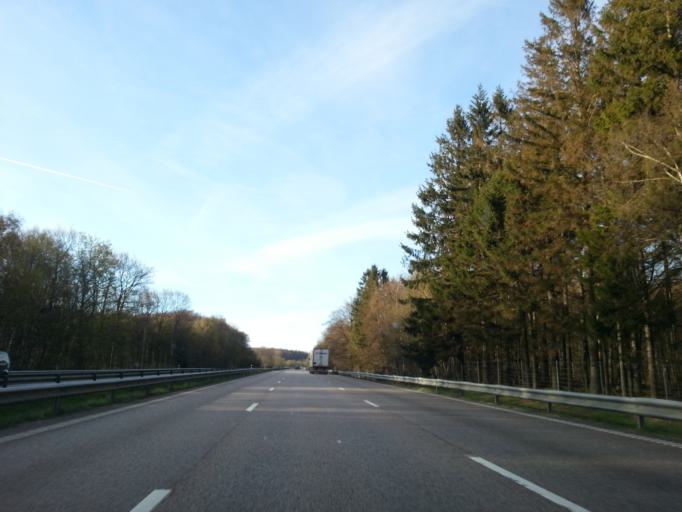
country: SE
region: Skane
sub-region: Angelholms Kommun
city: Munka-Ljungby
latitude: 56.3277
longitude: 12.9151
